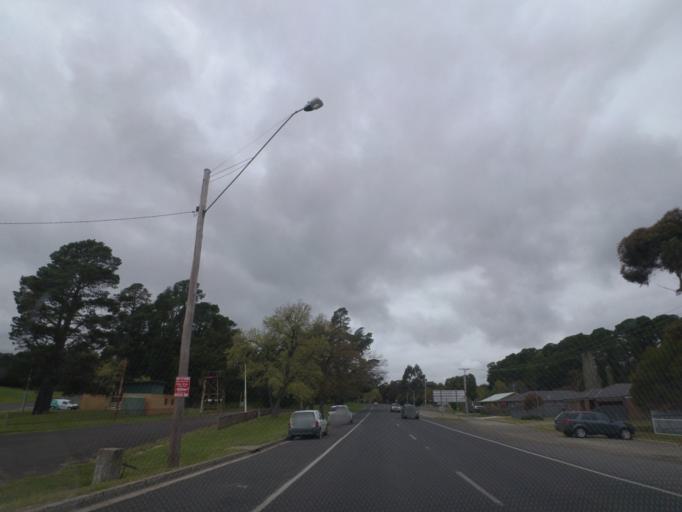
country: AU
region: Victoria
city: Brown Hill
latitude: -37.4190
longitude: 143.8959
